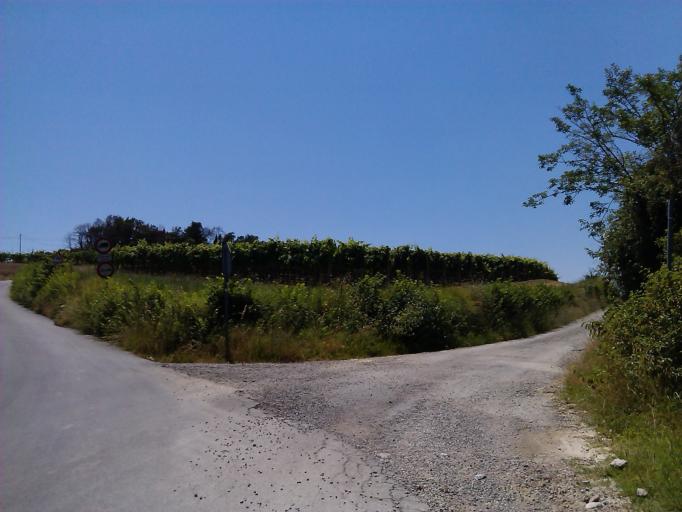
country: IT
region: Umbria
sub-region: Provincia di Terni
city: Fabro Scalo
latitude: 42.8532
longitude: 12.0410
